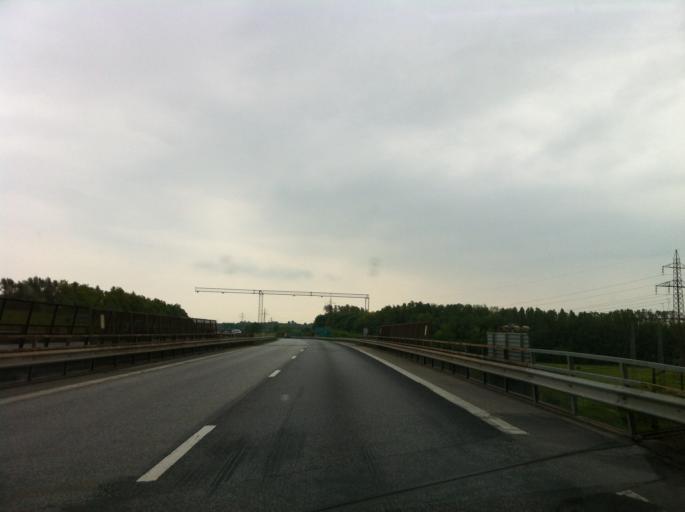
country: SE
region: Skane
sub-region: Burlovs Kommun
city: Arloev
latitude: 55.6520
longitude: 13.0981
